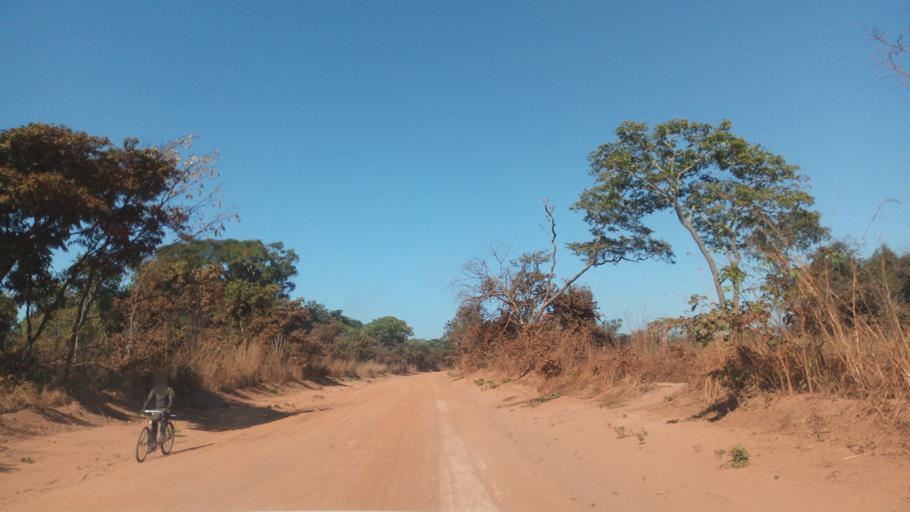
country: ZM
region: Luapula
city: Mwense
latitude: -10.7525
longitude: 28.3239
